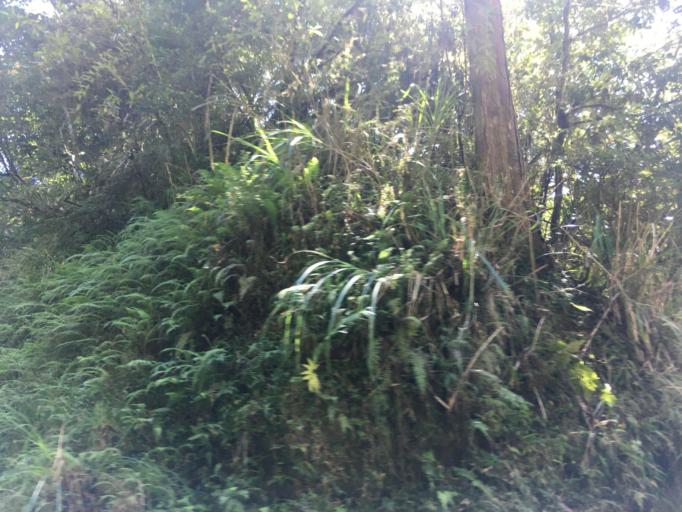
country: TW
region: Taiwan
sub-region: Yilan
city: Yilan
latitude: 24.6199
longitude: 121.4734
